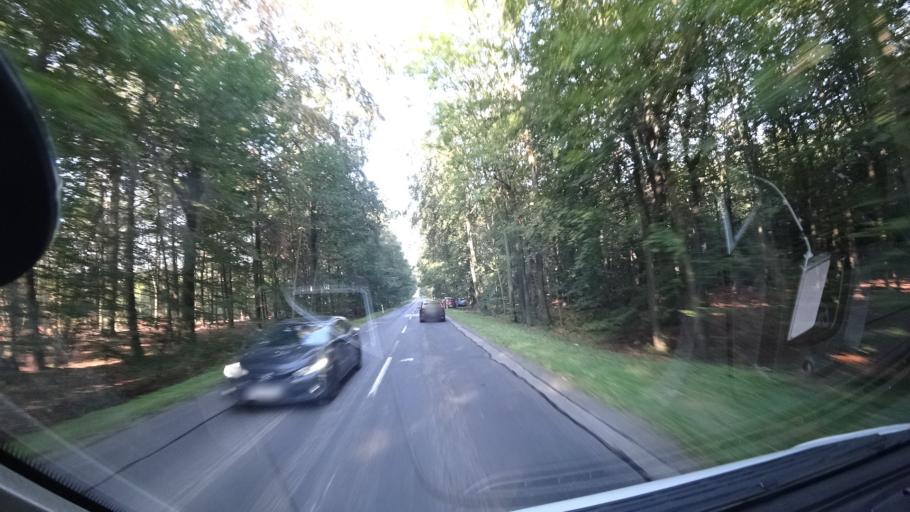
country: PL
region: Silesian Voivodeship
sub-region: Powiat gliwicki
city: Sosnicowice
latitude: 50.2795
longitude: 18.4940
